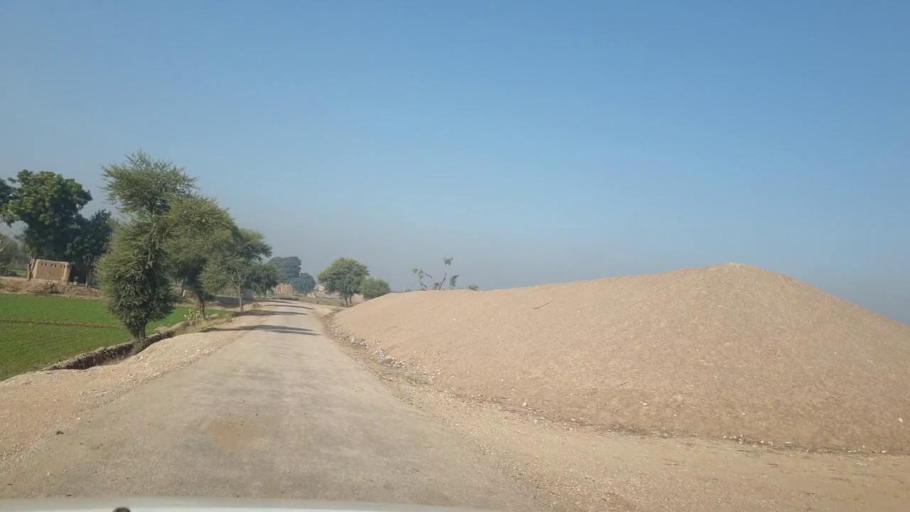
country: PK
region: Sindh
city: Dadu
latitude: 26.6782
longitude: 67.8120
